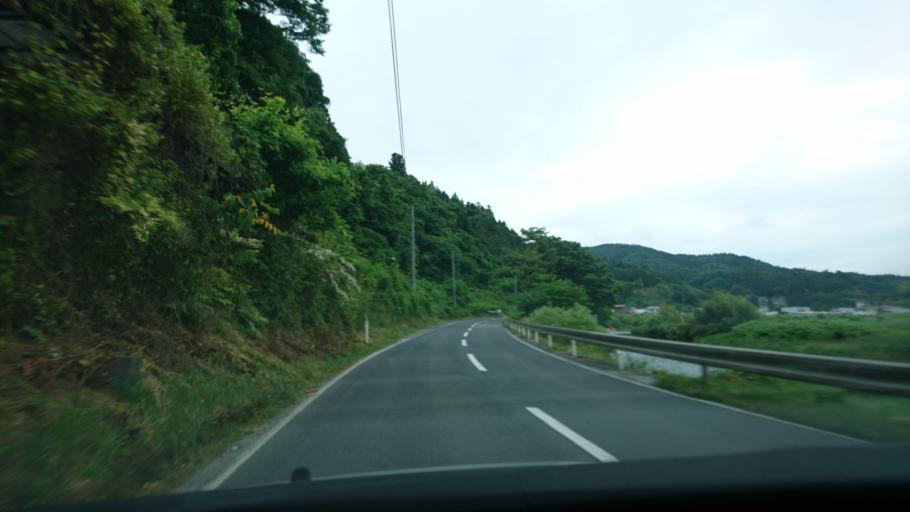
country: JP
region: Iwate
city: Ichinoseki
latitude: 38.9708
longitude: 141.2395
